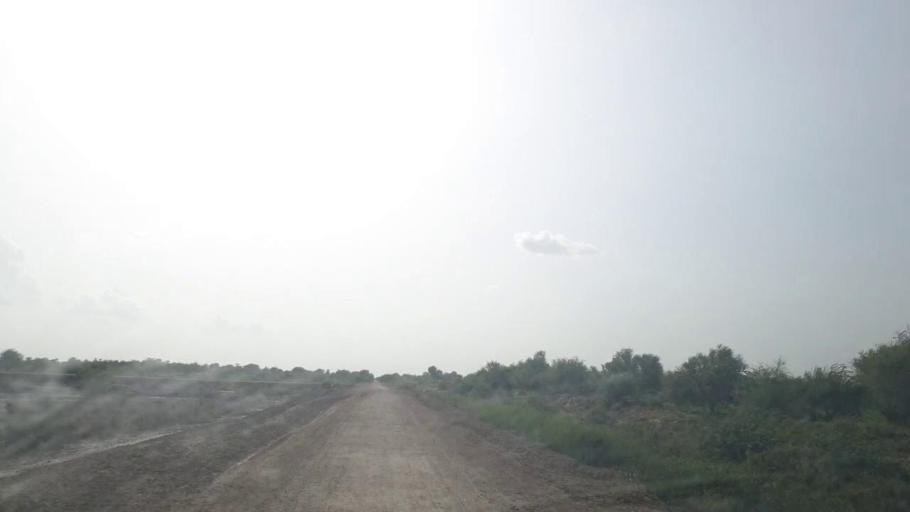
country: PK
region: Sindh
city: Tando Bago
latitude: 24.8256
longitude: 69.1222
